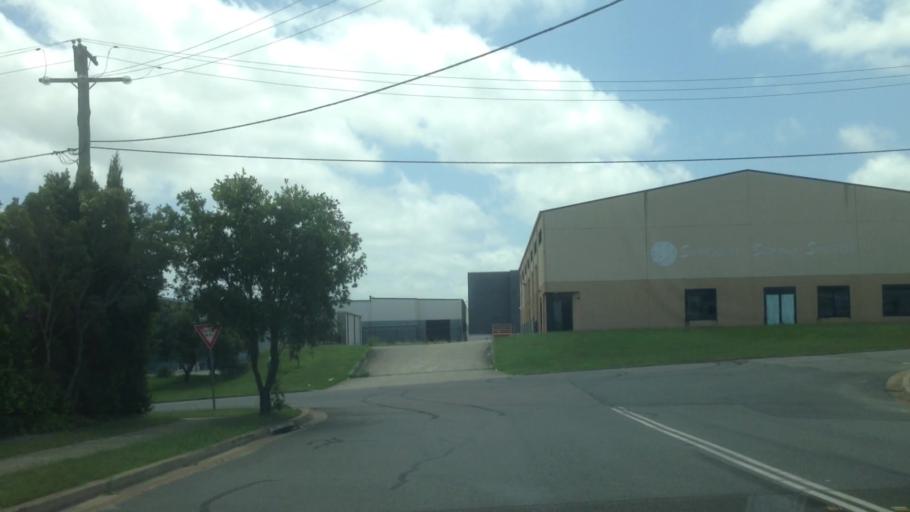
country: AU
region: New South Wales
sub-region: Lake Macquarie Shire
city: Dora Creek
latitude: -33.1181
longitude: 151.4735
